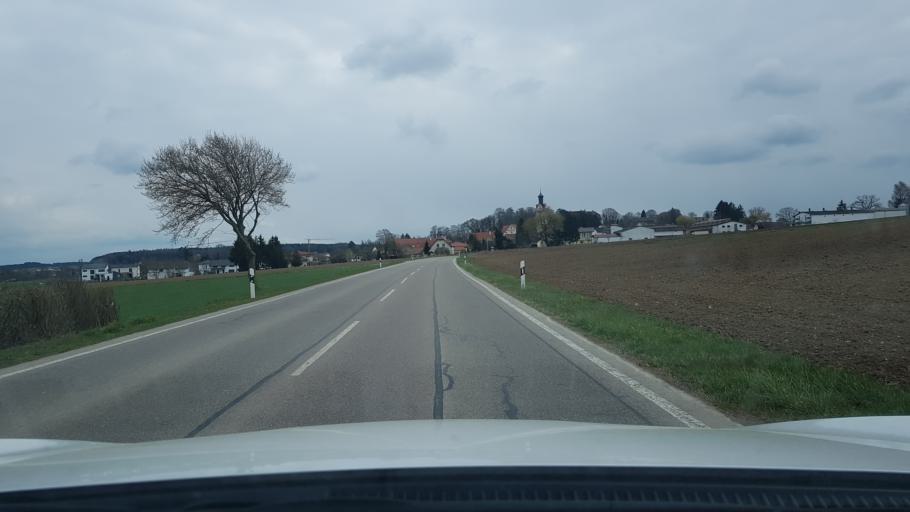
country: DE
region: Baden-Wuerttemberg
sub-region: Tuebingen Region
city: Oberstadion
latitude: 48.1916
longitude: 9.6901
